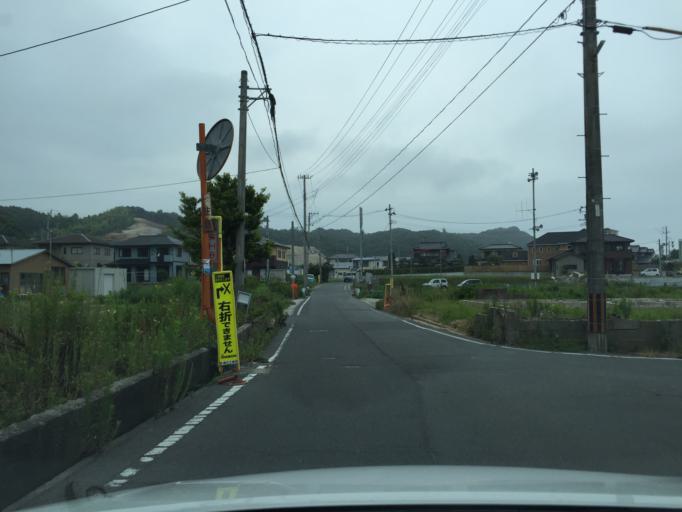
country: JP
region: Fukushima
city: Iwaki
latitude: 36.9768
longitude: 140.9653
